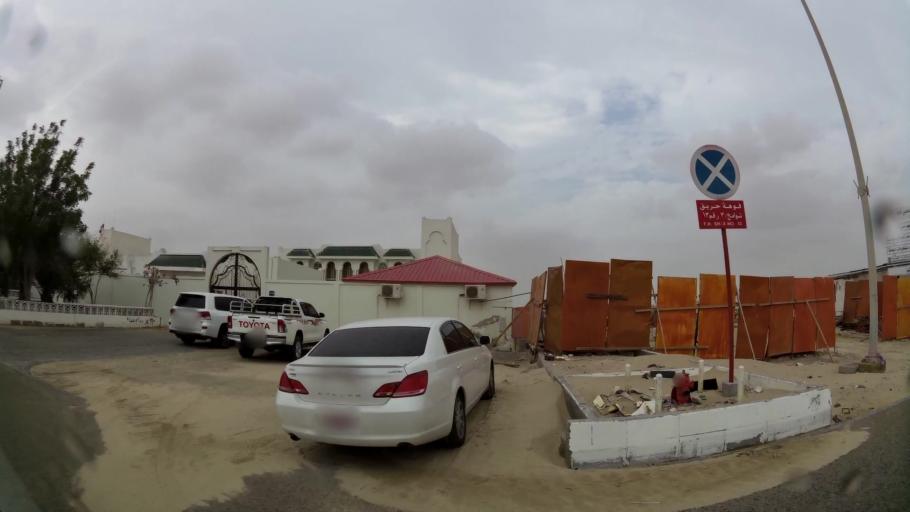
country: AE
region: Abu Dhabi
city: Abu Dhabi
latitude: 24.3625
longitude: 54.6585
